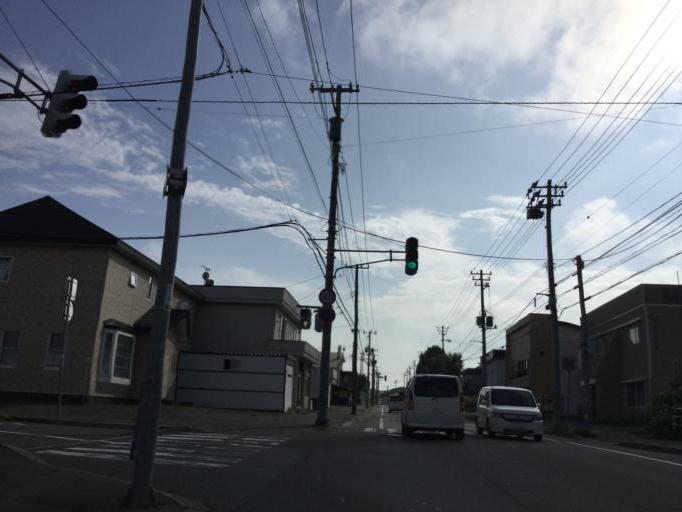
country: JP
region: Hokkaido
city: Wakkanai
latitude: 45.3906
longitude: 141.6801
